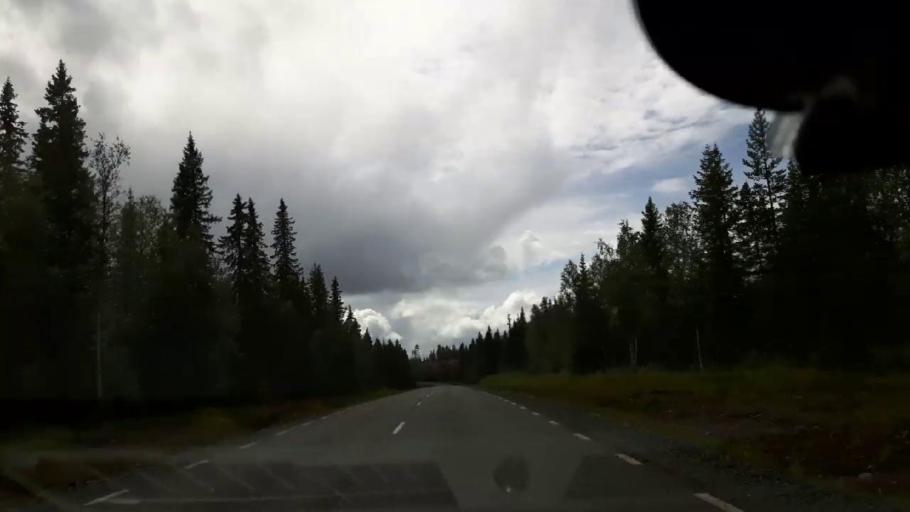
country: SE
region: Jaemtland
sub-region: Krokoms Kommun
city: Valla
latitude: 63.4779
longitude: 13.8519
